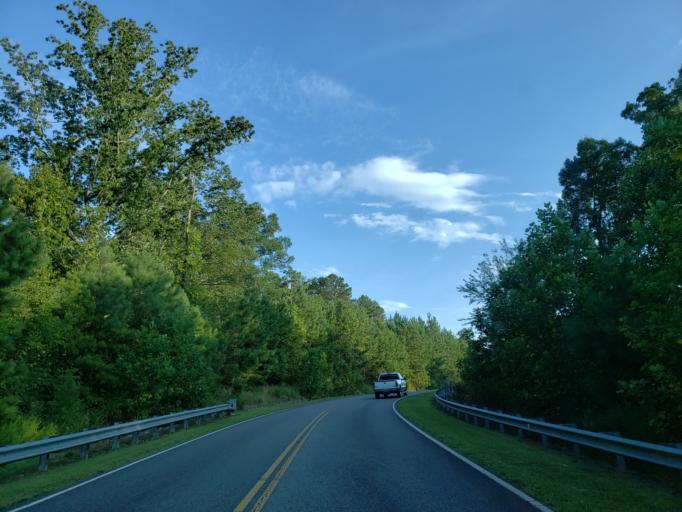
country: US
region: Georgia
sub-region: Cherokee County
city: Canton
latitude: 34.2253
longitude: -84.5737
